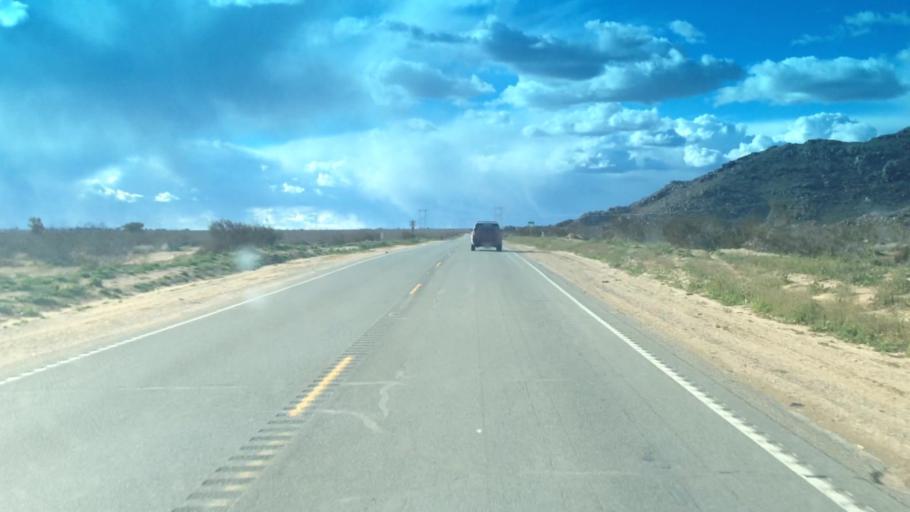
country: US
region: California
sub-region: San Bernardino County
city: Lucerne Valley
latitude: 34.4514
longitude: -117.0563
